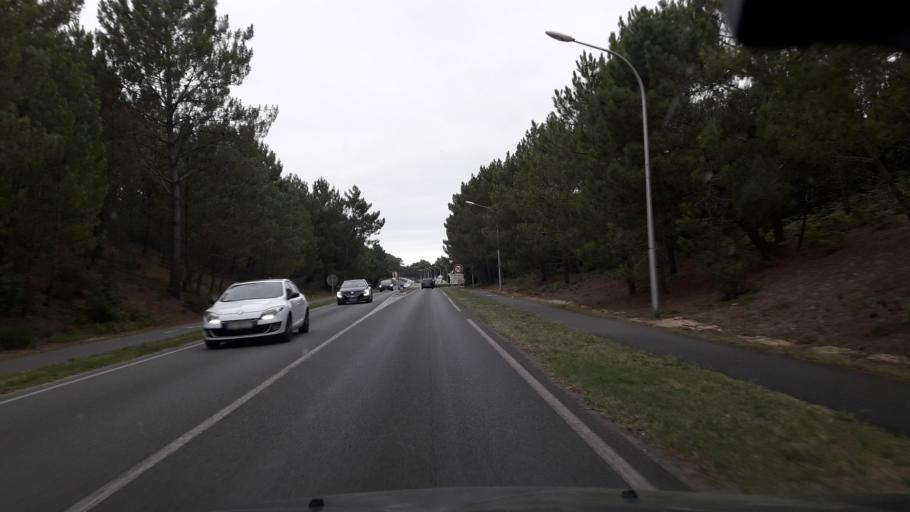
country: FR
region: Poitou-Charentes
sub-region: Departement de la Charente-Maritime
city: Les Mathes
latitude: 45.7051
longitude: -1.1653
